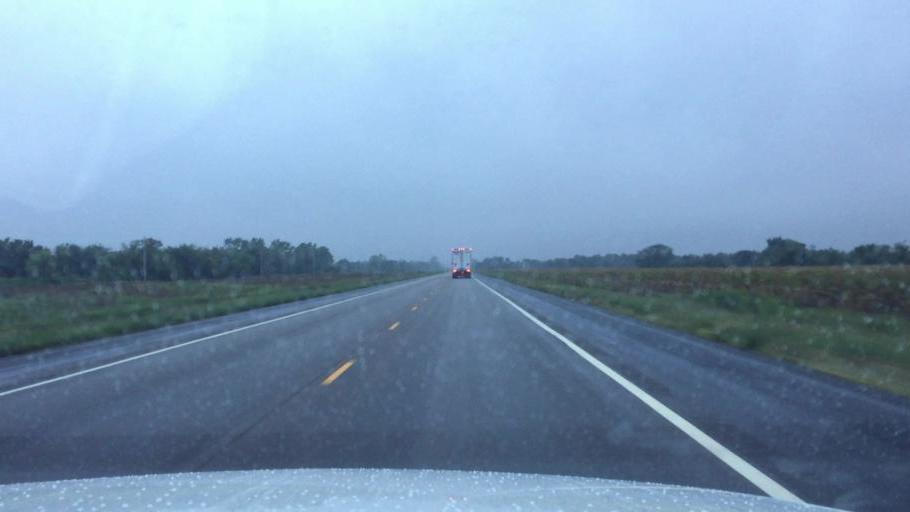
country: US
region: Kansas
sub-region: Montgomery County
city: Cherryvale
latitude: 37.4039
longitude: -95.5022
